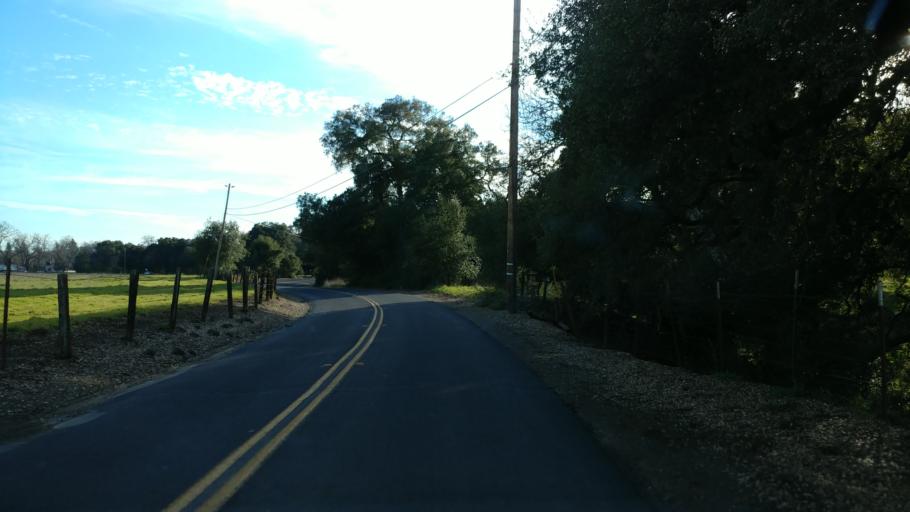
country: US
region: California
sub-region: Contra Costa County
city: Blackhawk
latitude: 37.8079
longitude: -121.8591
